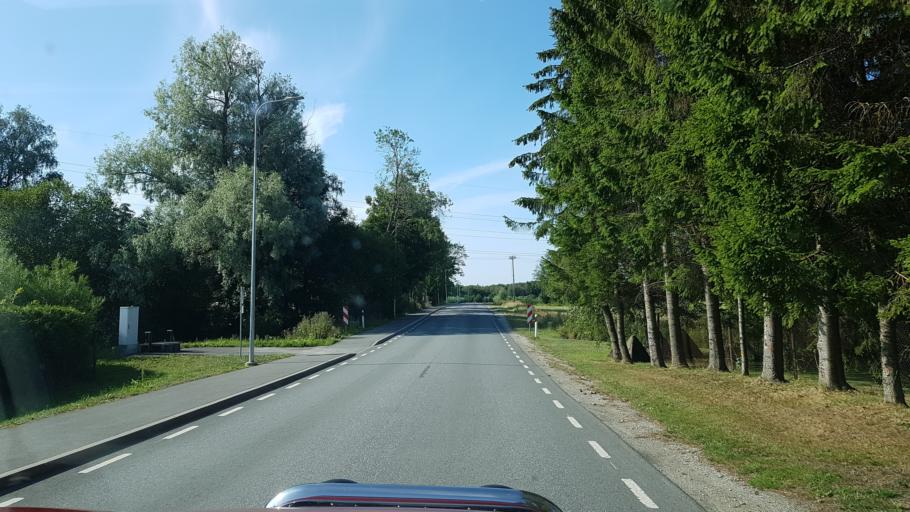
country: EE
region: Harju
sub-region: Joelaehtme vald
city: Loo
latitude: 59.3880
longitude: 24.9350
